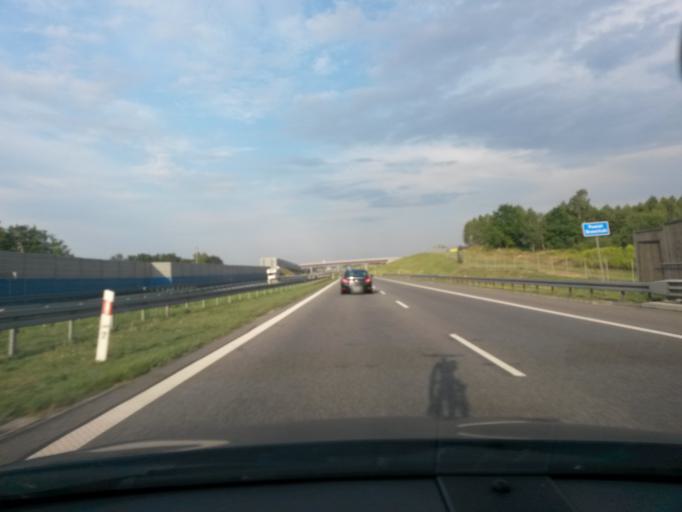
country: PL
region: Lodz Voivodeship
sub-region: Powiat zgierski
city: Strykow
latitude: 51.8966
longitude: 19.6794
